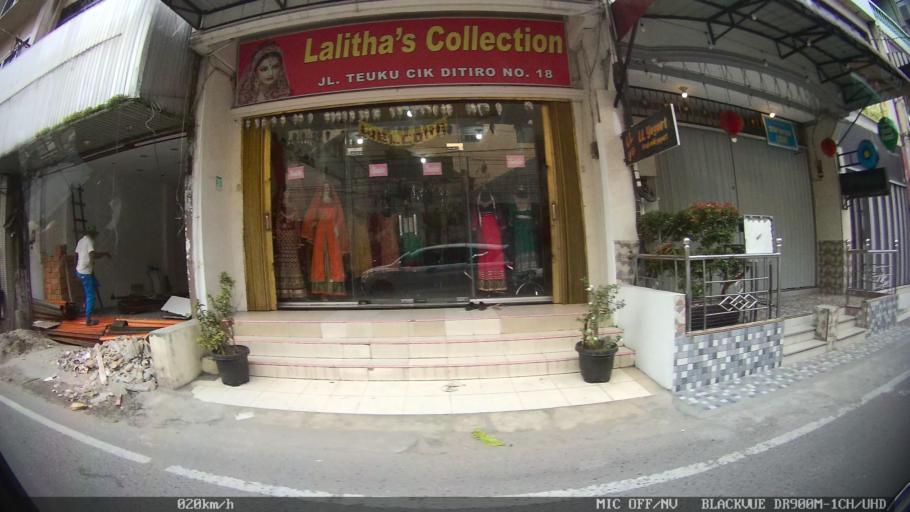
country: ID
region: North Sumatra
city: Medan
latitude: 3.5834
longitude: 98.6691
